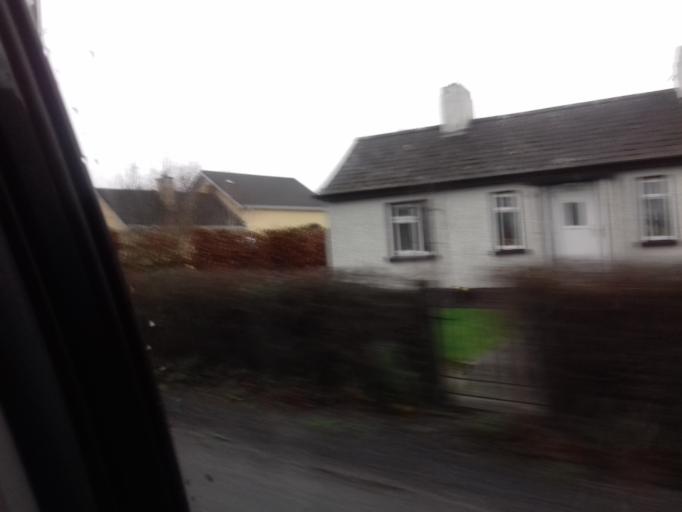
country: IE
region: Leinster
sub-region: County Carlow
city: Bagenalstown
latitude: 52.6712
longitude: -7.0105
